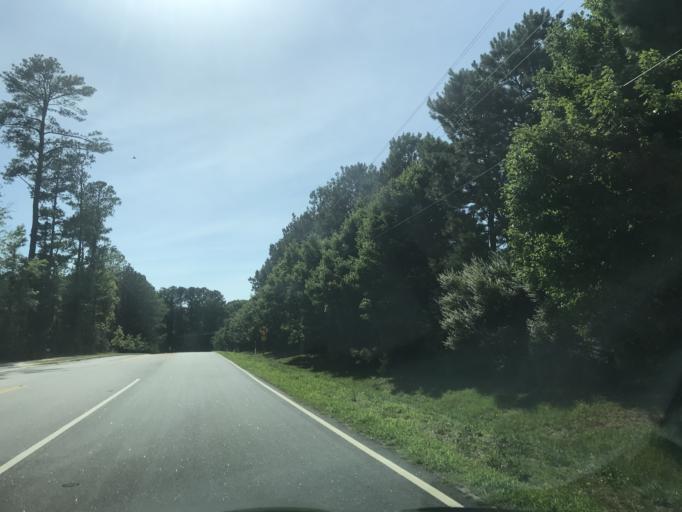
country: US
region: North Carolina
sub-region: Wake County
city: Garner
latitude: 35.7121
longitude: -78.6381
